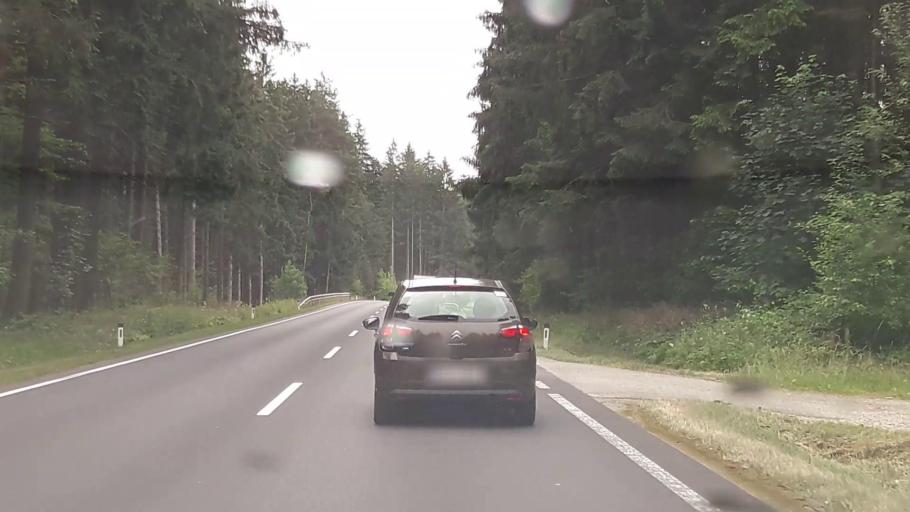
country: AT
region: Upper Austria
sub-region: Politischer Bezirk Rohrbach
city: Kleinzell im Muehlkreis
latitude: 48.4506
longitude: 14.0369
